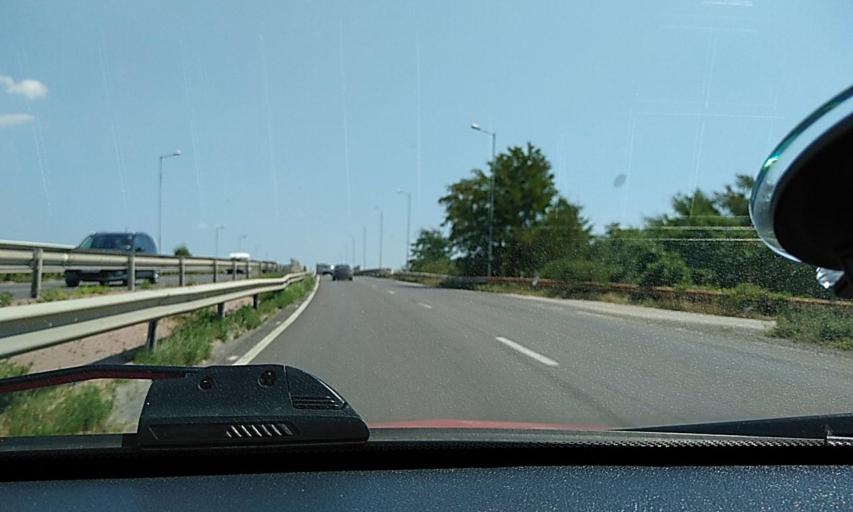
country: RO
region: Prahova
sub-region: Comuna Barcanesti
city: Tatarani
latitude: 44.8945
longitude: 26.0201
